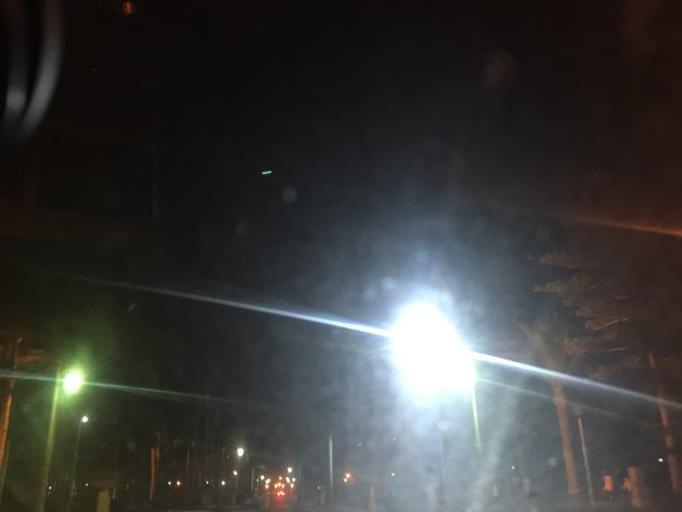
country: EG
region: Alexandria
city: Alexandria
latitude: 31.2859
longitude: 30.0164
